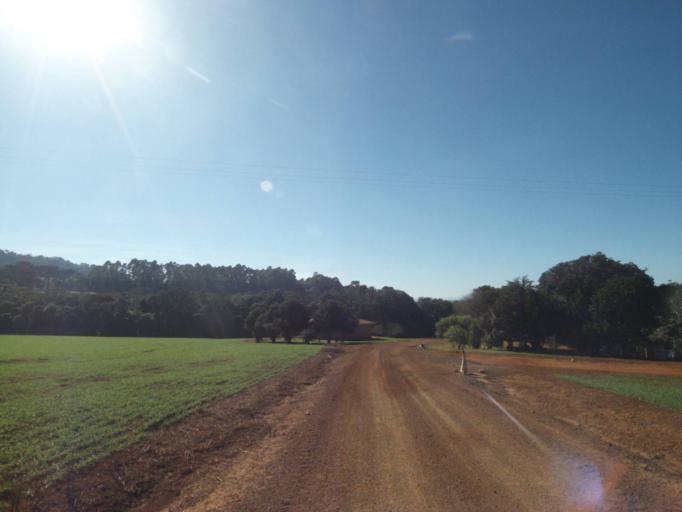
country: BR
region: Parana
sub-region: Tibagi
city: Tibagi
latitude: -24.3890
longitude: -50.3268
